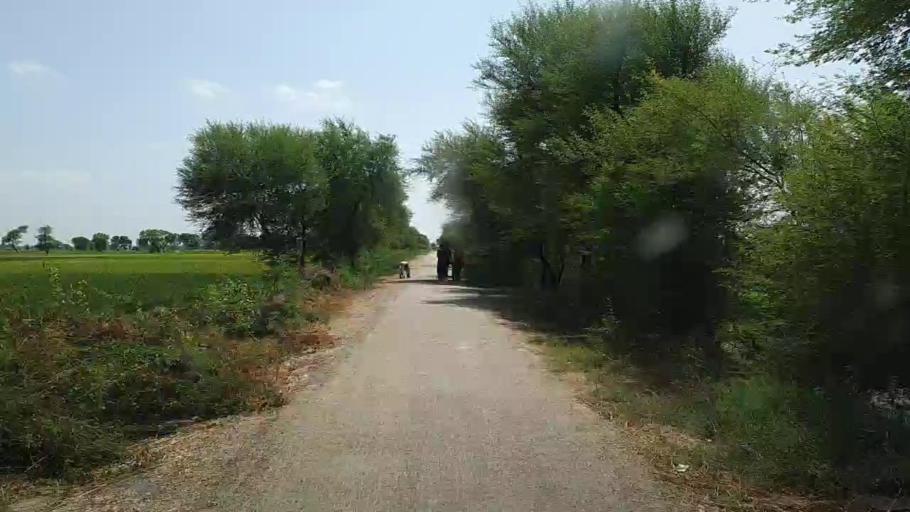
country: PK
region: Sindh
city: Kario
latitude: 24.6495
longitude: 68.5641
